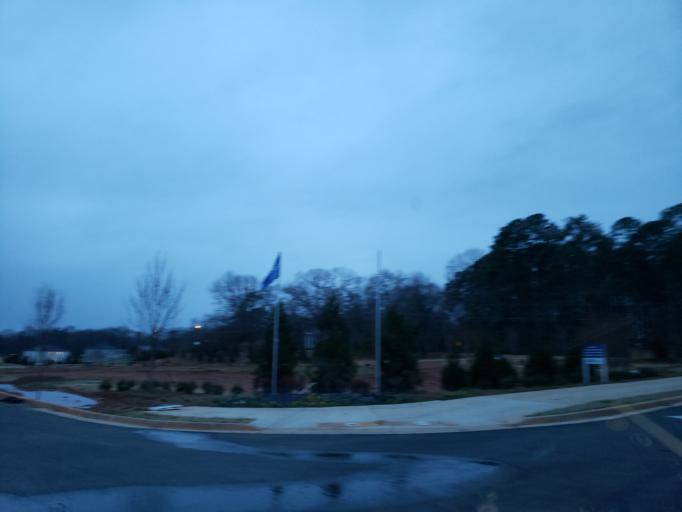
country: US
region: Georgia
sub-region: Cobb County
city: Mableton
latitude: 33.8413
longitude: -84.5793
